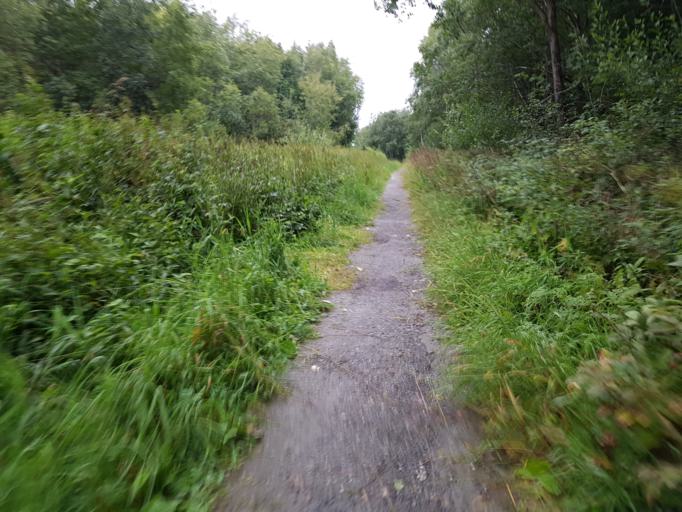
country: NO
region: Sor-Trondelag
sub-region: Trondheim
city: Trondheim
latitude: 63.4018
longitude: 10.4597
